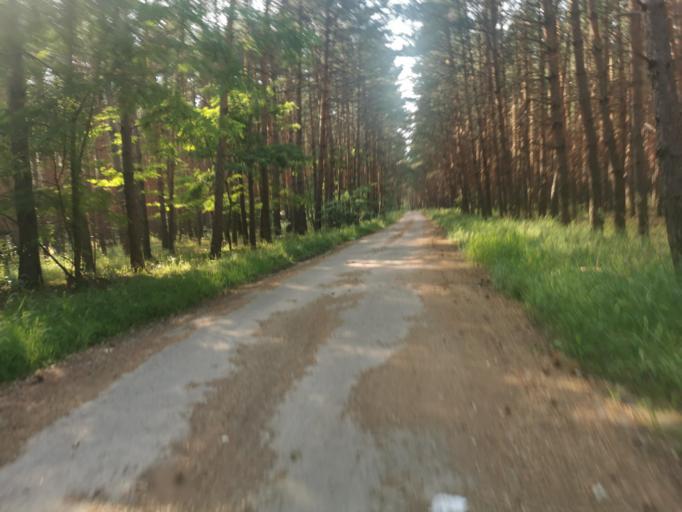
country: CZ
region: South Moravian
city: Ratiskovice
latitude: 48.9170
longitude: 17.2115
